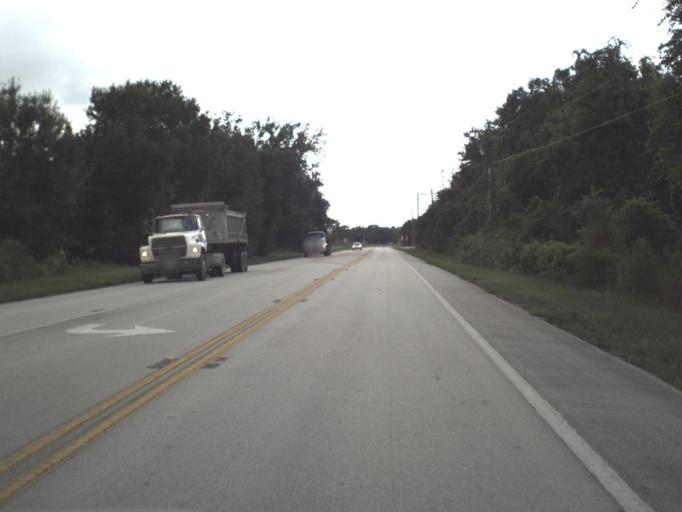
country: US
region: Florida
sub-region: Hardee County
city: Zolfo Springs
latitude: 27.5092
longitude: -81.7666
